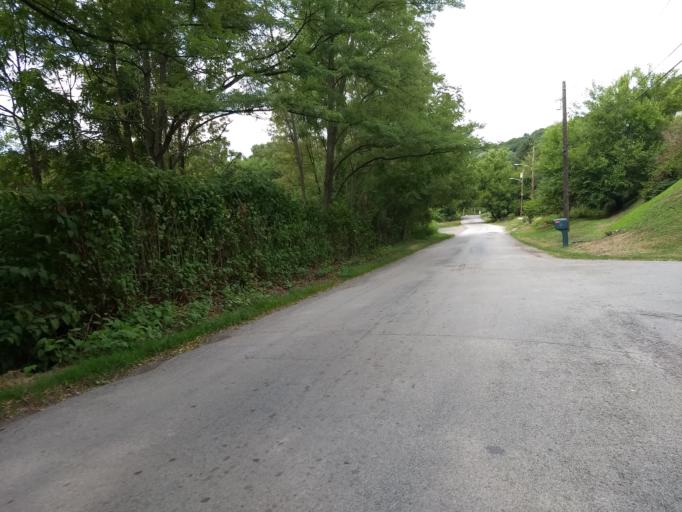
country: US
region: Pennsylvania
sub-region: Allegheny County
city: Brackenridge
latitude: 40.6133
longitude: -79.7116
